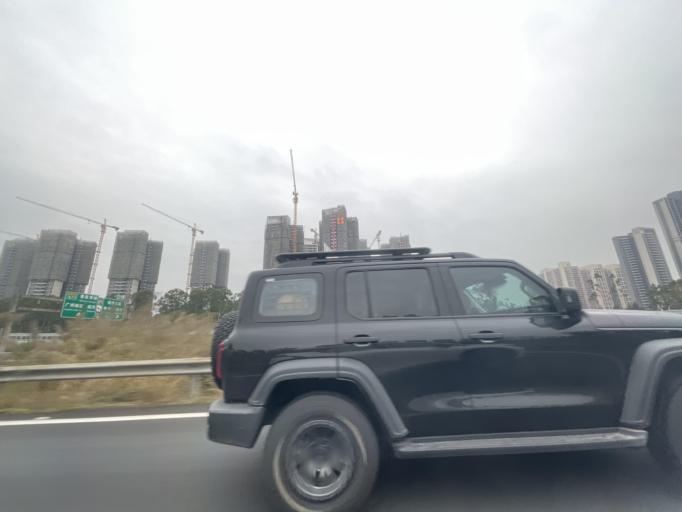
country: CN
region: Guangdong
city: Huangge
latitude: 22.7910
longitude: 113.5084
